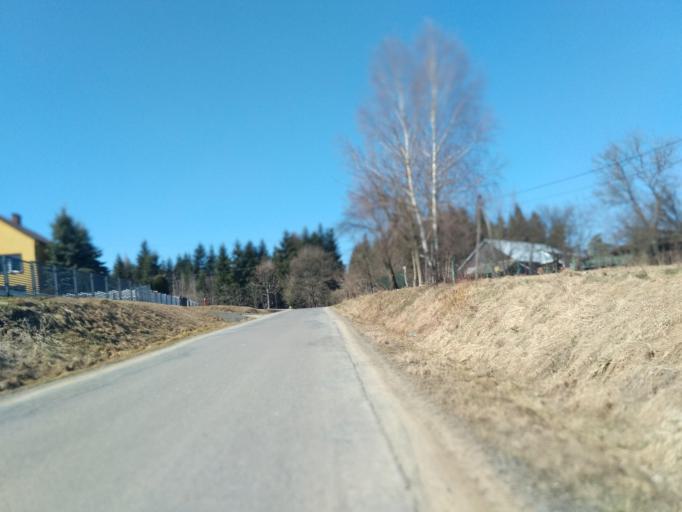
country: PL
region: Subcarpathian Voivodeship
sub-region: Powiat debicki
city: Brzostek
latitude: 49.9571
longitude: 21.4276
